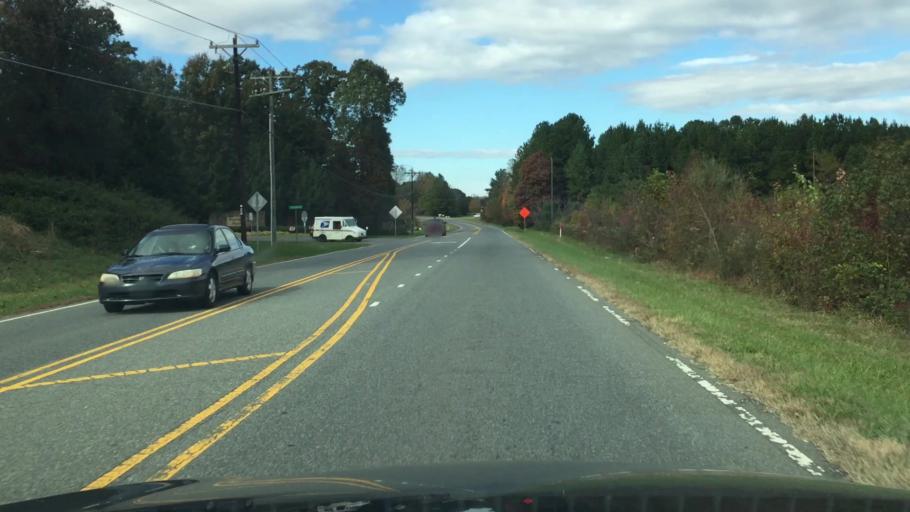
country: US
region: North Carolina
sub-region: Iredell County
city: Troutman
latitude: 35.6519
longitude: -80.8445
